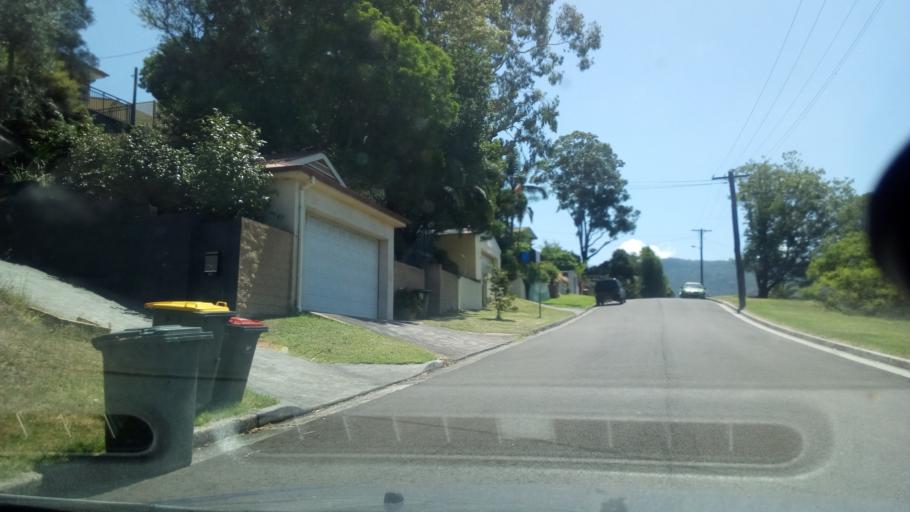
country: AU
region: New South Wales
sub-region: Wollongong
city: West Wollongong
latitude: -34.4300
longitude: 150.8595
